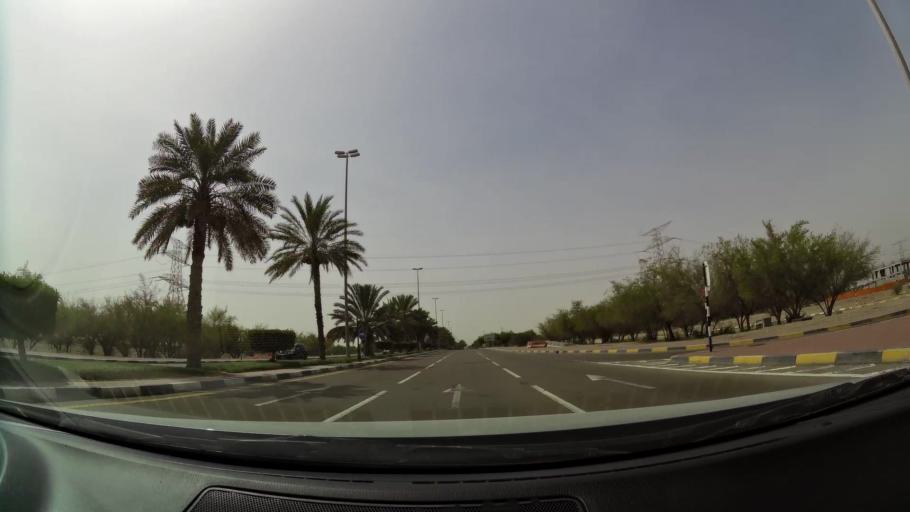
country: AE
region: Abu Dhabi
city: Al Ain
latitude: 24.1727
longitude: 55.6656
